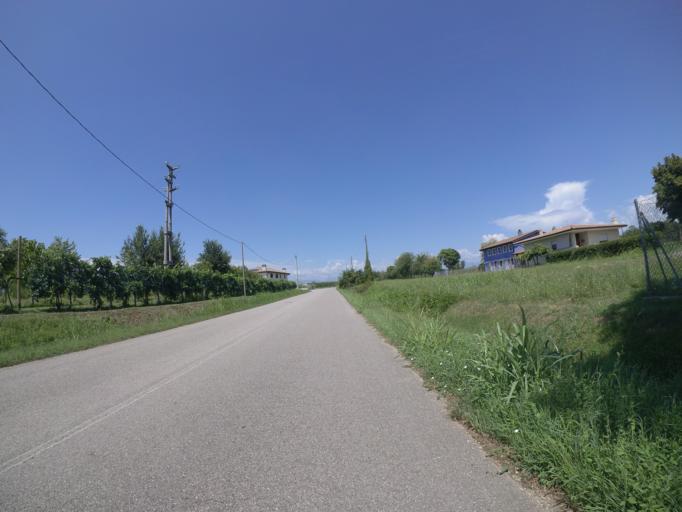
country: IT
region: Friuli Venezia Giulia
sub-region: Provincia di Udine
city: Talmassons
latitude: 45.9363
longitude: 13.1152
